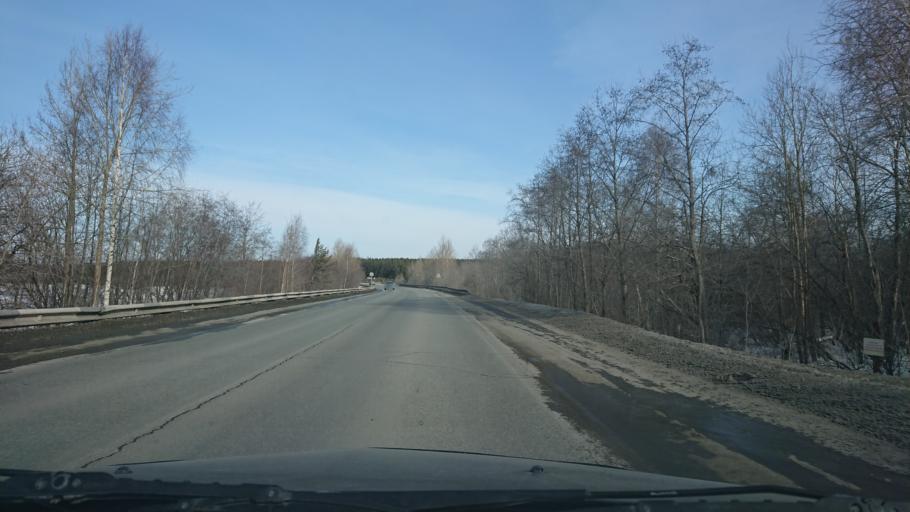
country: RU
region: Sverdlovsk
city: Revda
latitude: 56.8112
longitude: 59.9749
